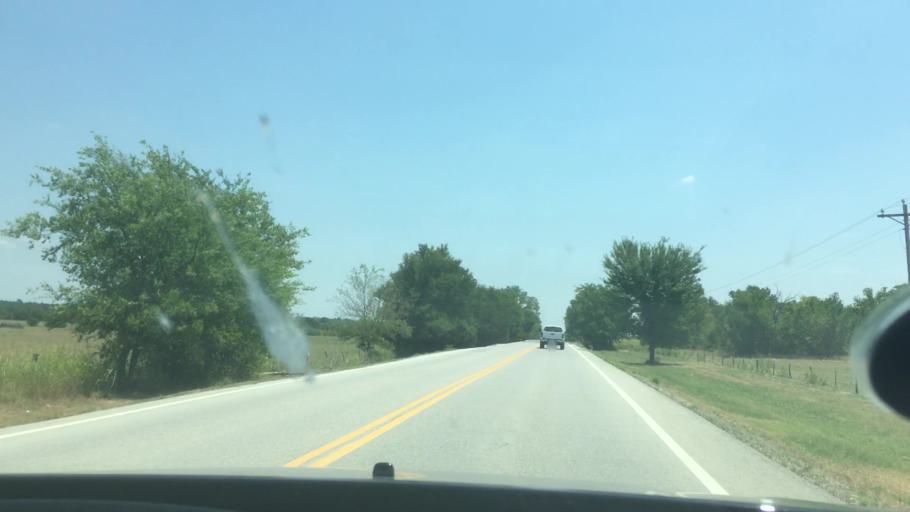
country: US
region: Oklahoma
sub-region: Bryan County
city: Durant
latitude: 34.1620
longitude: -96.3960
